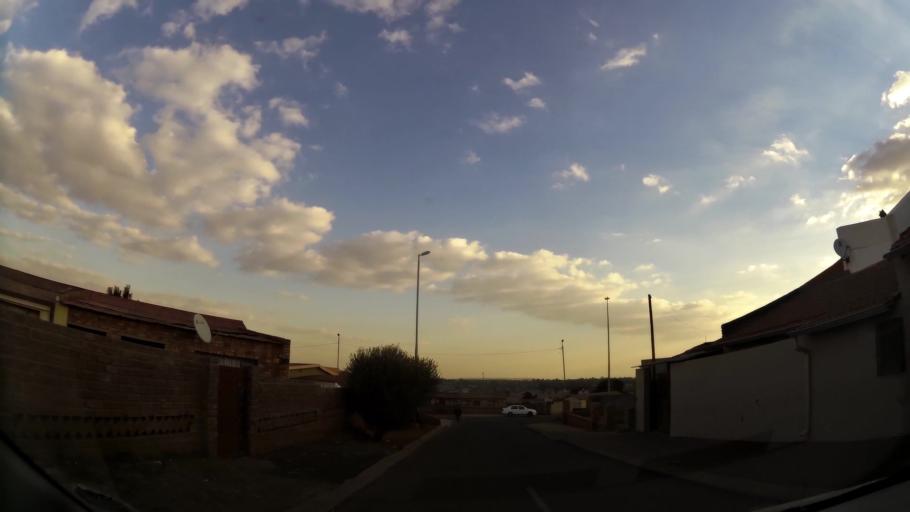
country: ZA
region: Gauteng
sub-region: West Rand District Municipality
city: Krugersdorp
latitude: -26.0806
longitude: 27.7558
